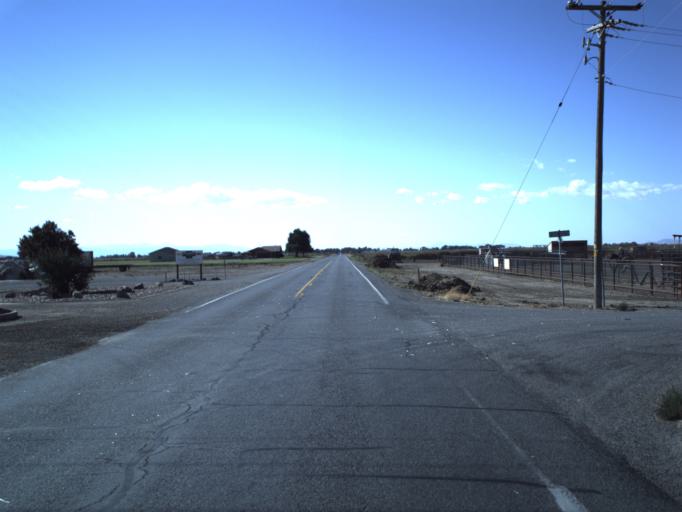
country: US
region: Utah
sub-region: Millard County
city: Delta
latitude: 39.3237
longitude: -112.6524
